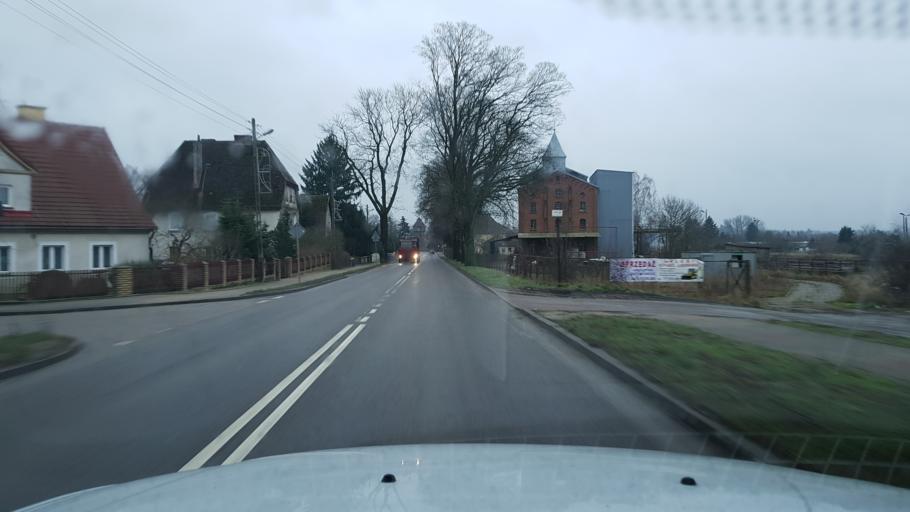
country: PL
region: West Pomeranian Voivodeship
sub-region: Powiat gryficki
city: Ploty
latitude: 53.8112
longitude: 15.2599
